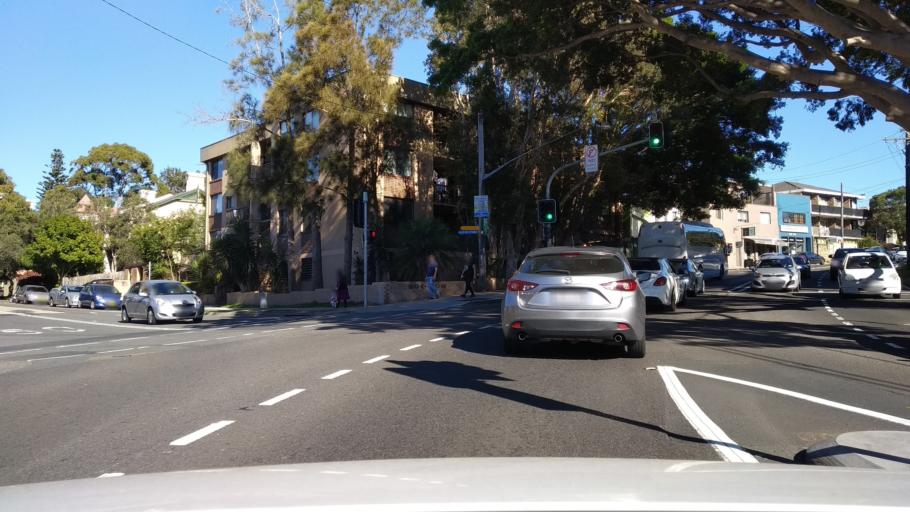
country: AU
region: New South Wales
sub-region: Waverley
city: Bondi
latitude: -33.8893
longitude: 151.2596
